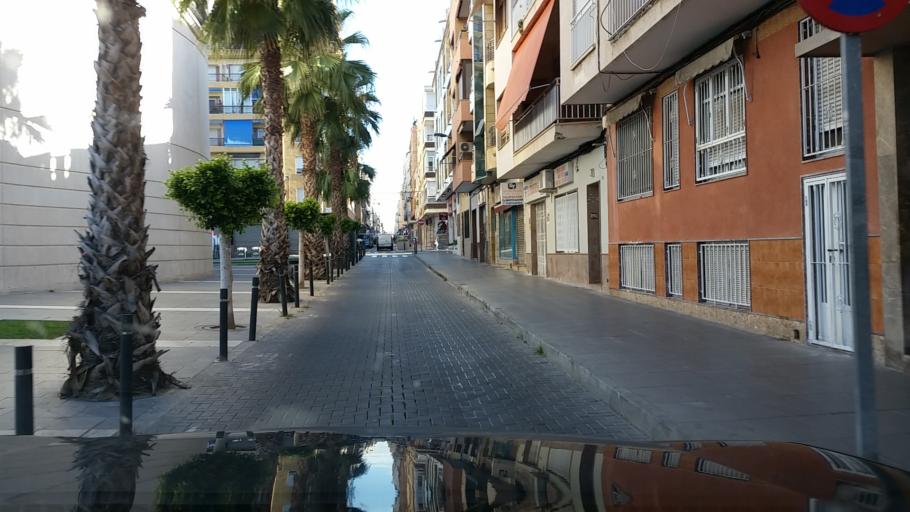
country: ES
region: Valencia
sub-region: Provincia de Alicante
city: Torrevieja
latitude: 37.9763
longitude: -0.6762
